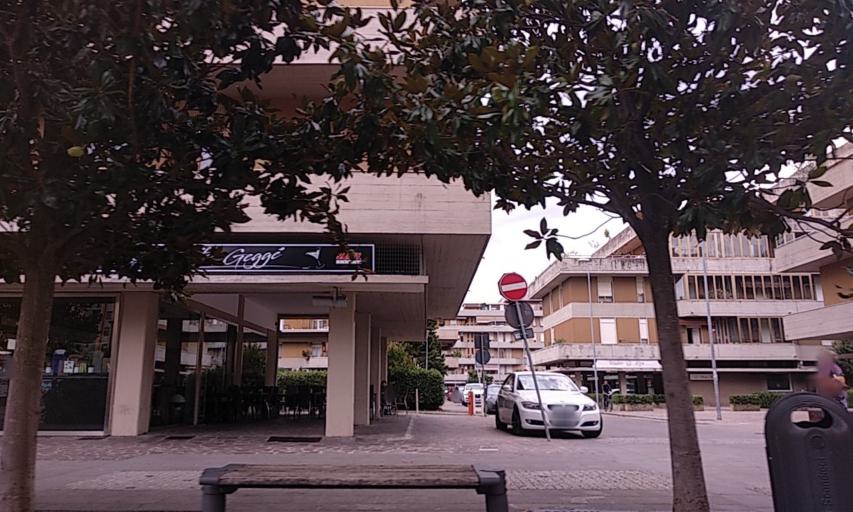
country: IT
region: Tuscany
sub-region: Province of Florence
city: Scandicci
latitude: 43.7563
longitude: 11.1850
